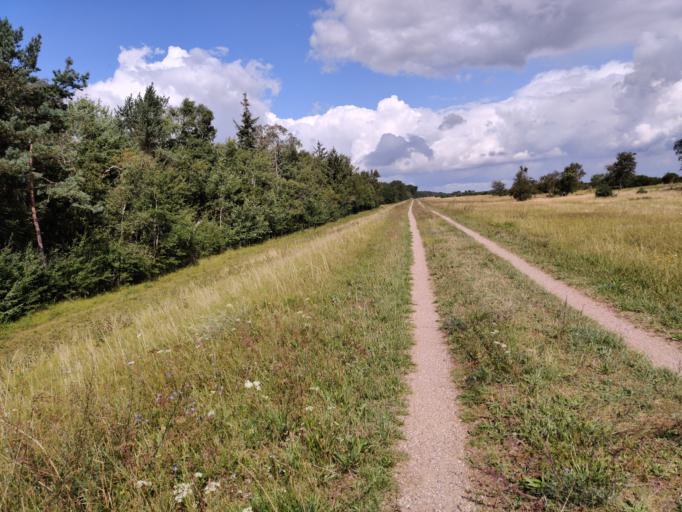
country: DK
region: Zealand
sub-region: Guldborgsund Kommune
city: Nykobing Falster
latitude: 54.6140
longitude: 11.9646
